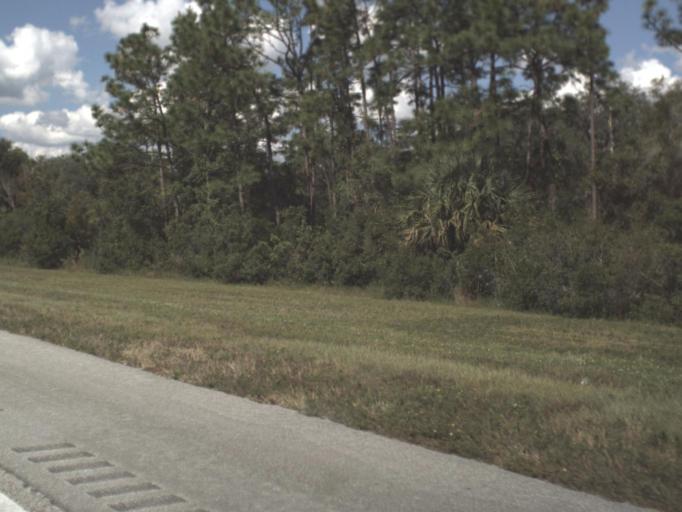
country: US
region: Florida
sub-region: Indian River County
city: Fellsmere
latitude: 27.7413
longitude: -80.9278
